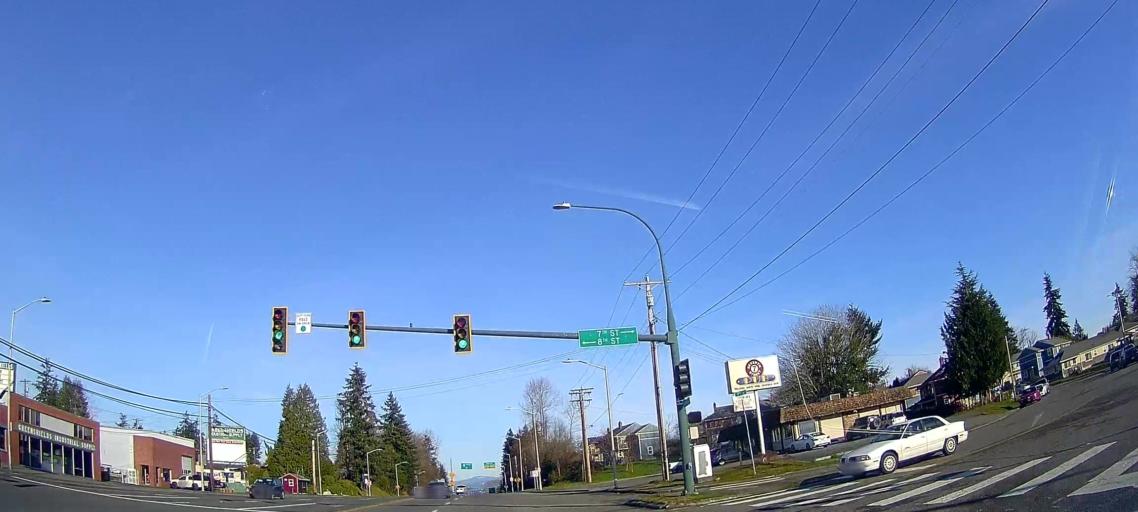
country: US
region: Washington
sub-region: Snohomish County
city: Everett
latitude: 48.0079
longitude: -122.1946
